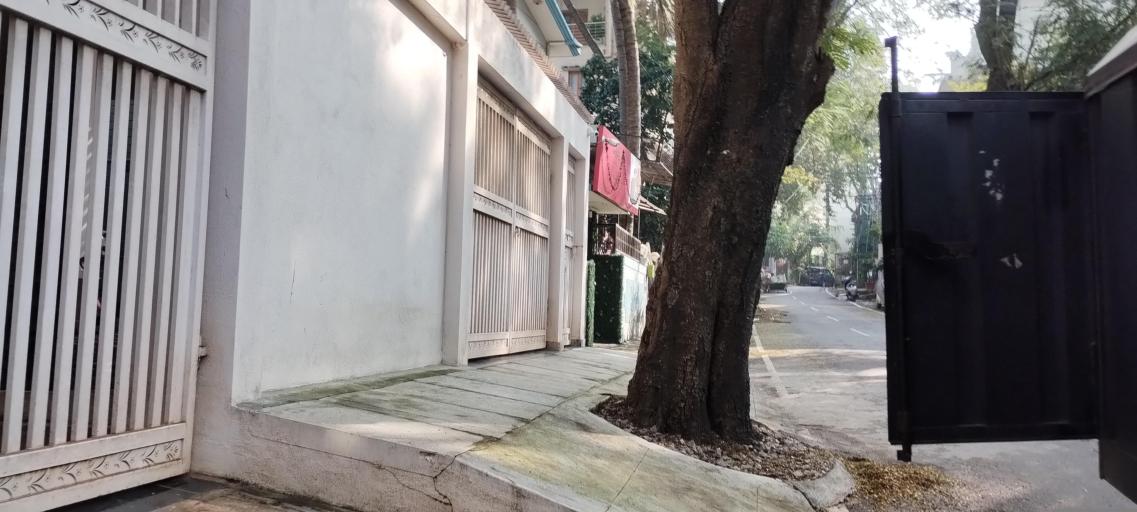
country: IN
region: Karnataka
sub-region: Bangalore Urban
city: Bangalore
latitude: 12.9361
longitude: 77.5411
